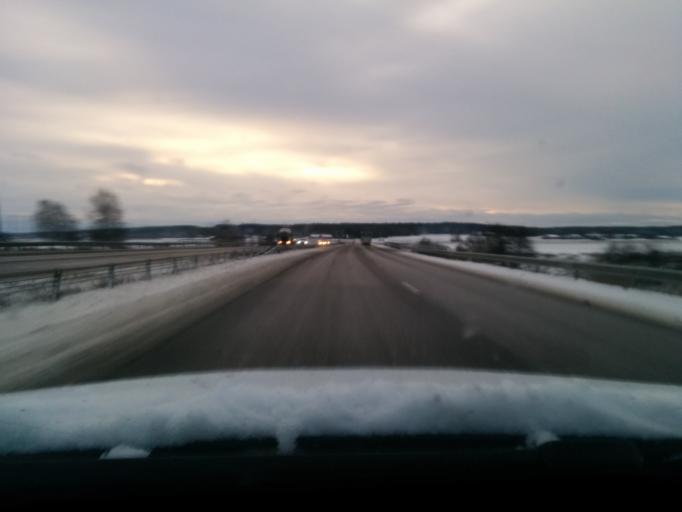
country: SE
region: Uppsala
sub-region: Uppsala Kommun
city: Saevja
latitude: 59.8164
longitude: 17.7545
